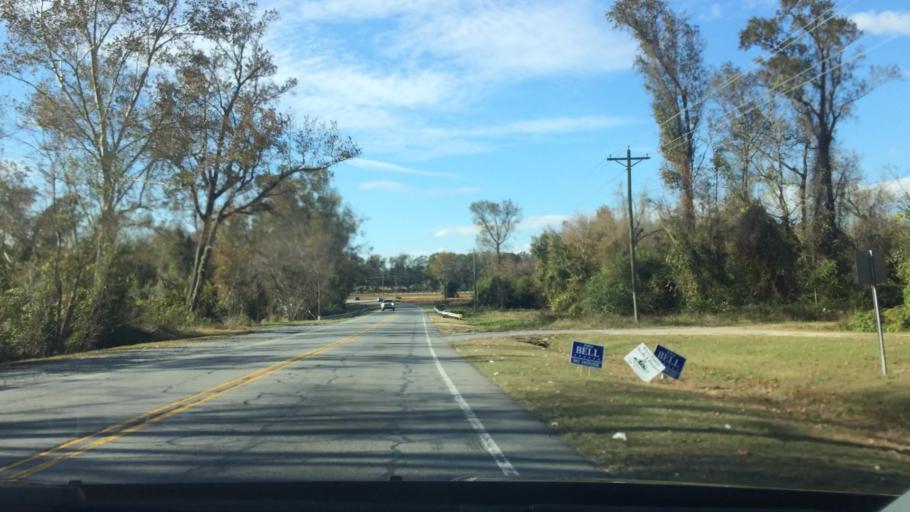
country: US
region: North Carolina
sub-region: Greene County
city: Snow Hill
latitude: 35.4574
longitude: -77.6976
